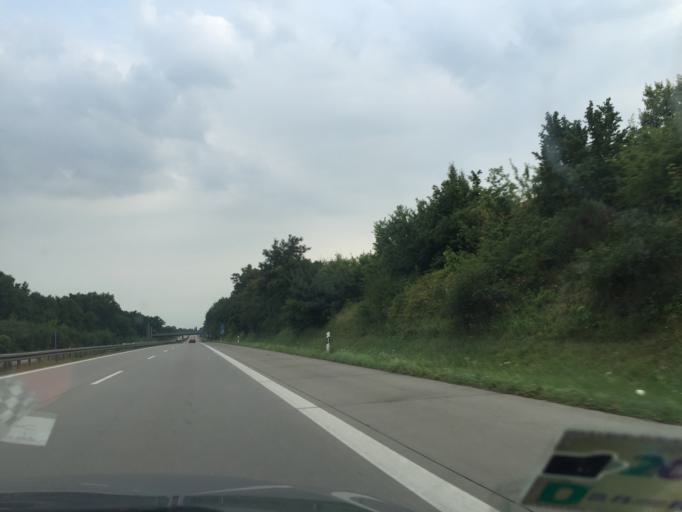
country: DE
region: Brandenburg
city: Bernau bei Berlin
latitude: 52.6962
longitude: 13.5553
